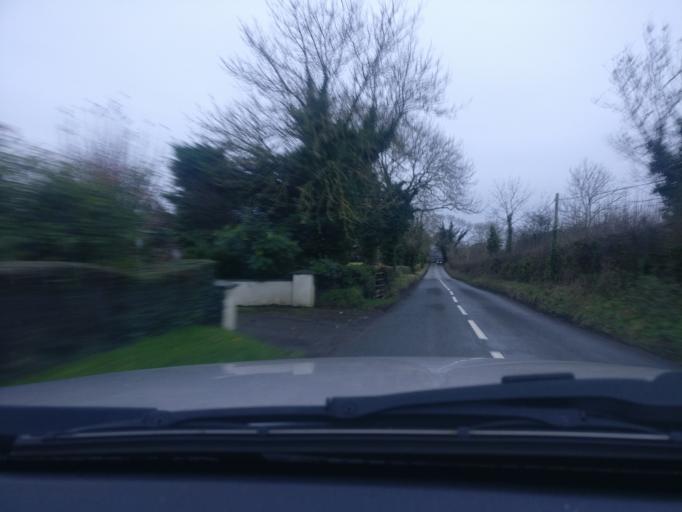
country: IE
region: Leinster
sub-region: Kildare
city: Kilcock
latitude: 53.4745
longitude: -6.6232
